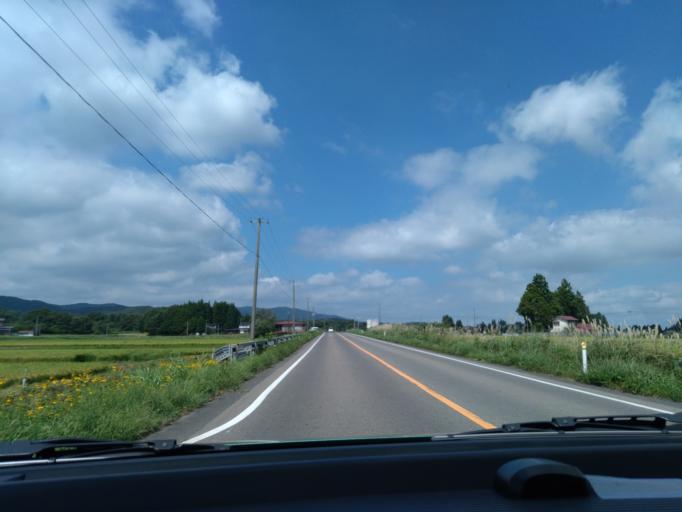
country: JP
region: Iwate
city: Hanamaki
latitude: 39.4642
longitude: 141.1015
